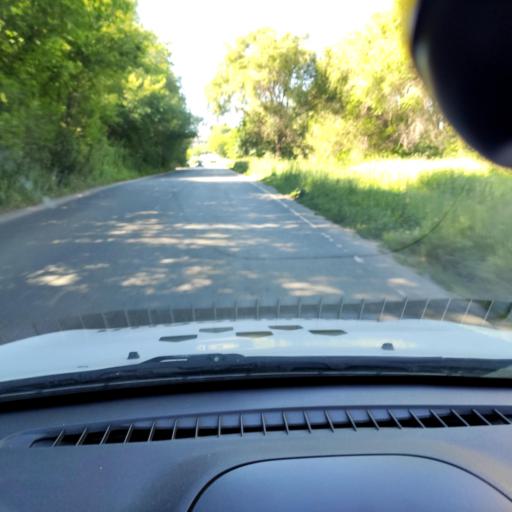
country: RU
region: Samara
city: Tol'yatti
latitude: 53.5760
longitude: 49.2549
